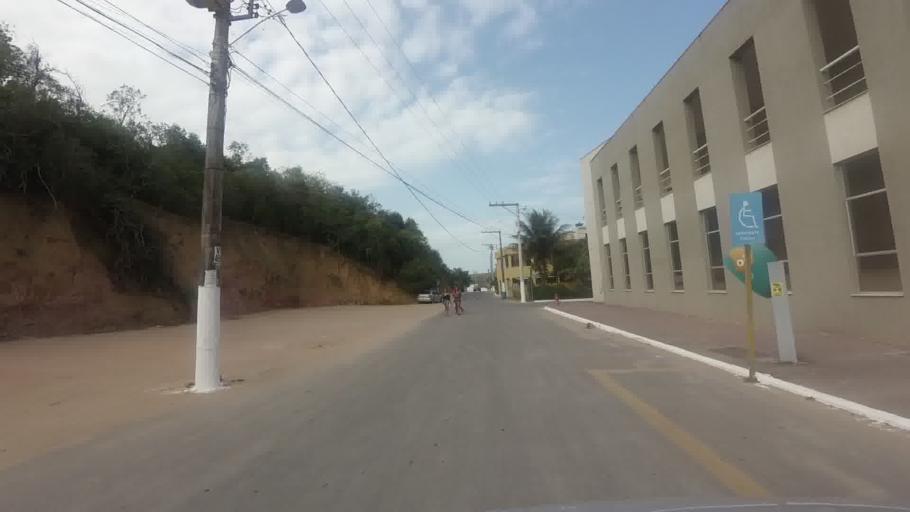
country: BR
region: Espirito Santo
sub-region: Itapemirim
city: Itapemirim
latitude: -21.0081
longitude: -40.8313
